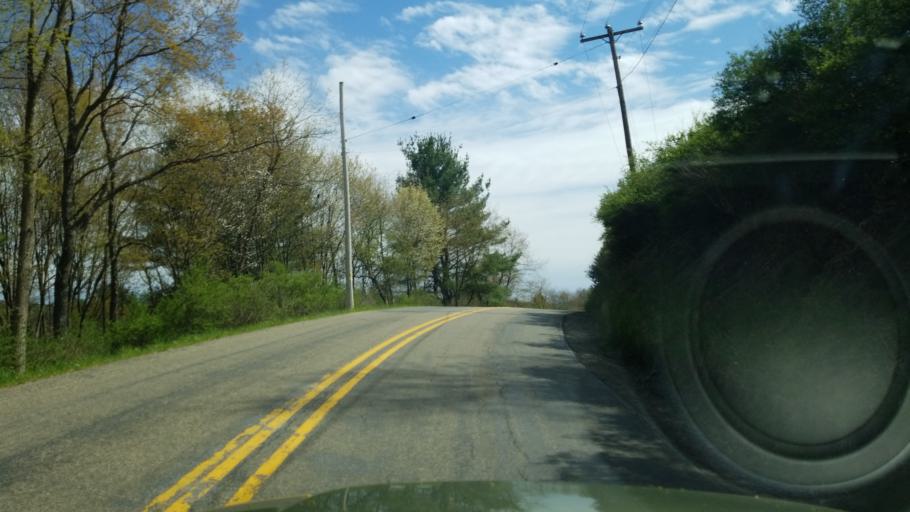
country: US
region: Pennsylvania
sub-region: Jefferson County
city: Brockway
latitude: 41.2304
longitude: -78.8508
